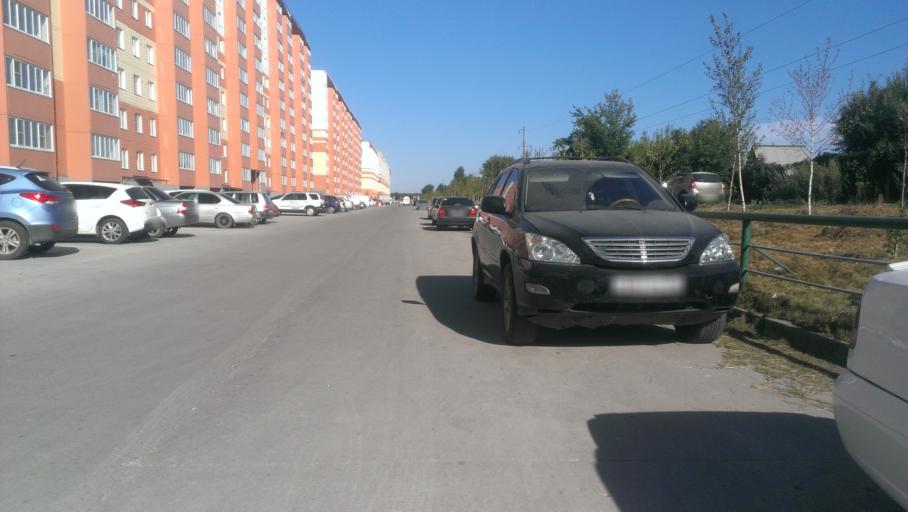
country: RU
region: Altai Krai
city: Novosilikatnyy
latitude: 53.3257
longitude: 83.6694
